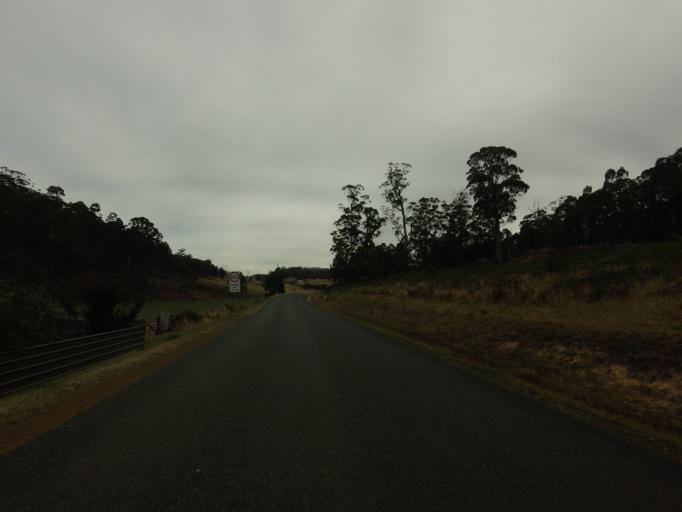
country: AU
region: Tasmania
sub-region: Sorell
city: Sorell
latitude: -42.5418
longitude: 147.5686
